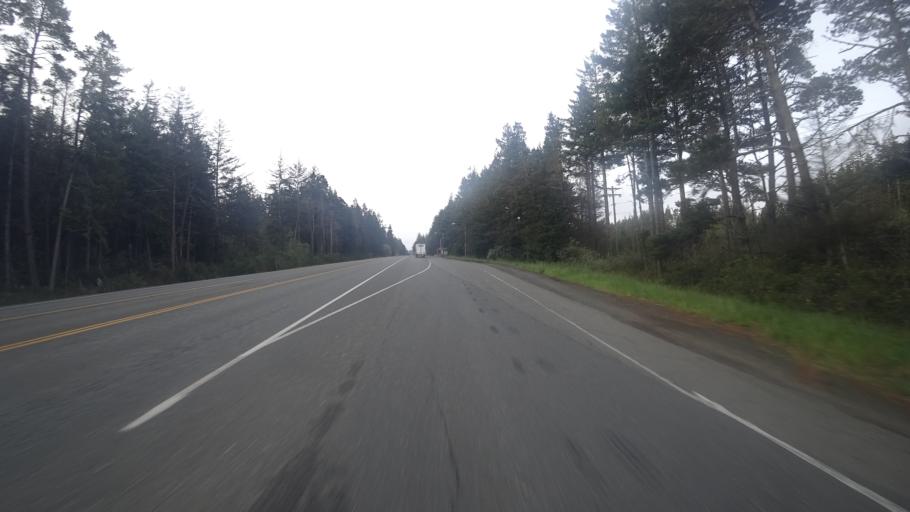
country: US
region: Oregon
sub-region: Coos County
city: Lakeside
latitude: 43.5141
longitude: -124.2173
